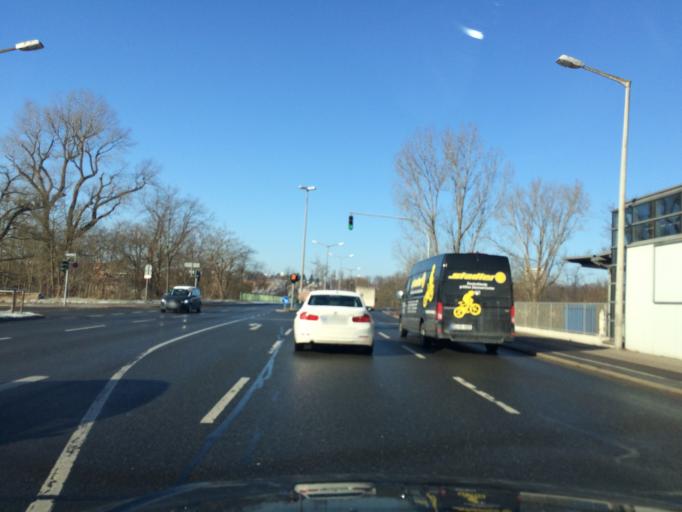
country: DE
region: Bavaria
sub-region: Regierungsbezirk Mittelfranken
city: Furth
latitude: 49.4820
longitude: 10.9867
